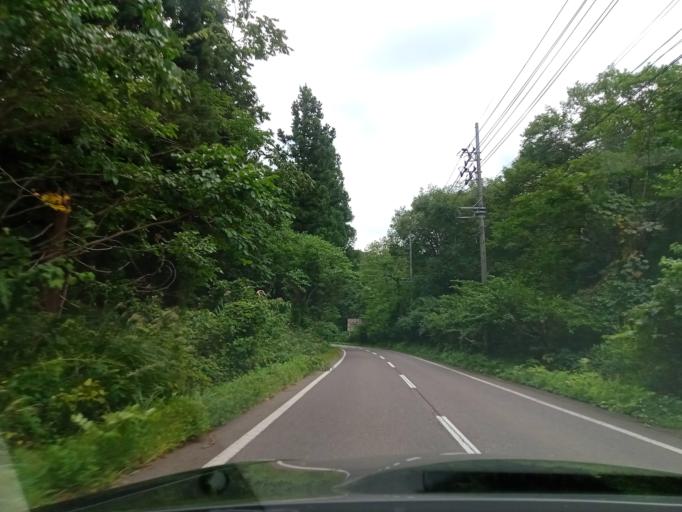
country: JP
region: Niigata
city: Arai
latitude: 36.8786
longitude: 138.1867
